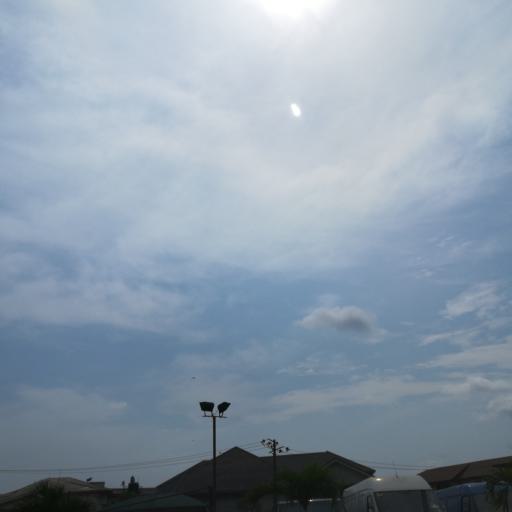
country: NG
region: Rivers
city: Port Harcourt
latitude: 4.8344
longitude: 7.0148
